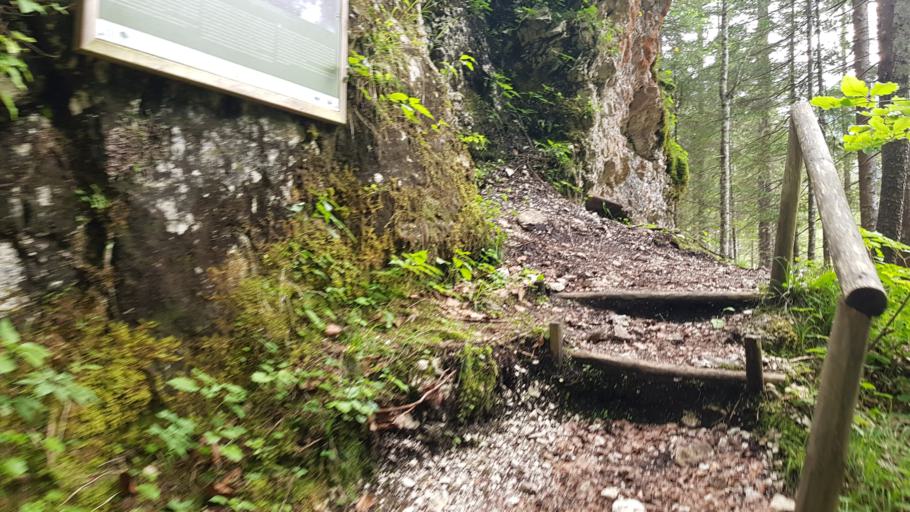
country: IT
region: Friuli Venezia Giulia
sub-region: Provincia di Udine
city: Malborghetto
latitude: 46.4590
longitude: 13.4870
